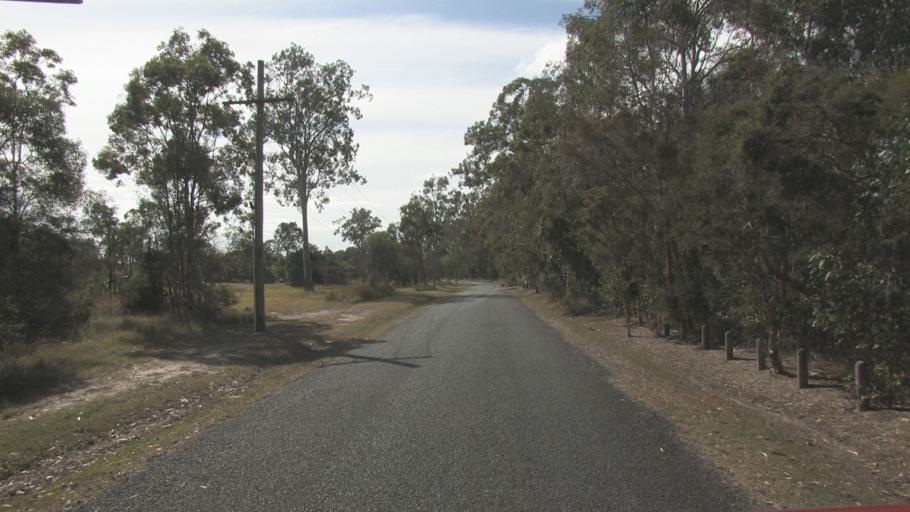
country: AU
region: Queensland
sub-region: Logan
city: Woodridge
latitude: -27.6655
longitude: 153.0847
